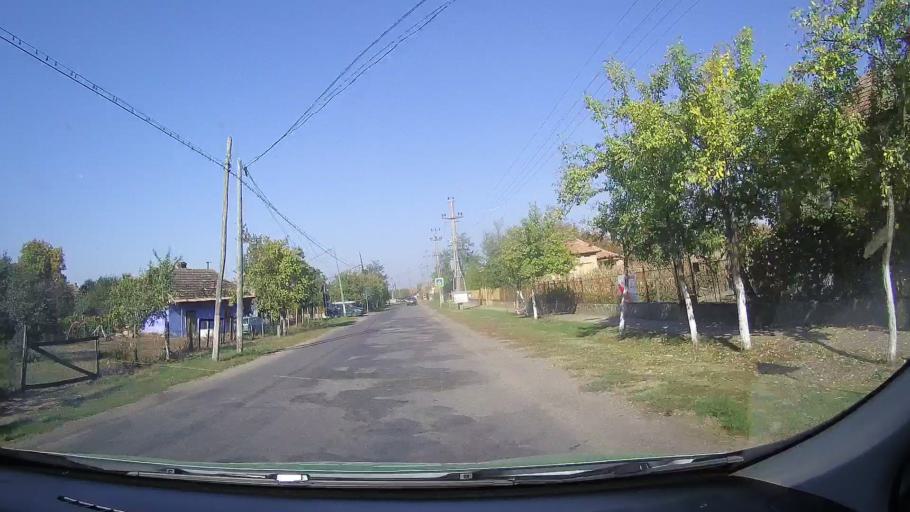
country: RO
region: Satu Mare
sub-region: Comuna Sanislau
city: Sanislau
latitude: 47.6307
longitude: 22.3326
